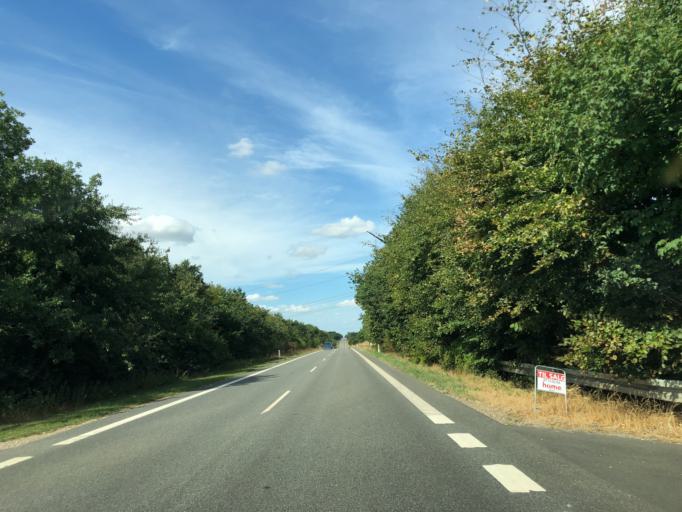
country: DK
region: Central Jutland
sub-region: Ikast-Brande Kommune
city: Bording Kirkeby
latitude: 56.1381
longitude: 9.3196
